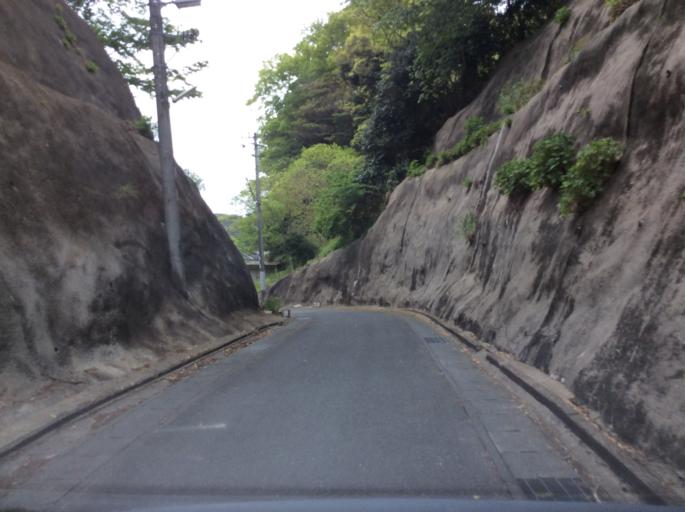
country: JP
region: Ibaraki
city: Kitaibaraki
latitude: 36.8538
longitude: 140.7947
